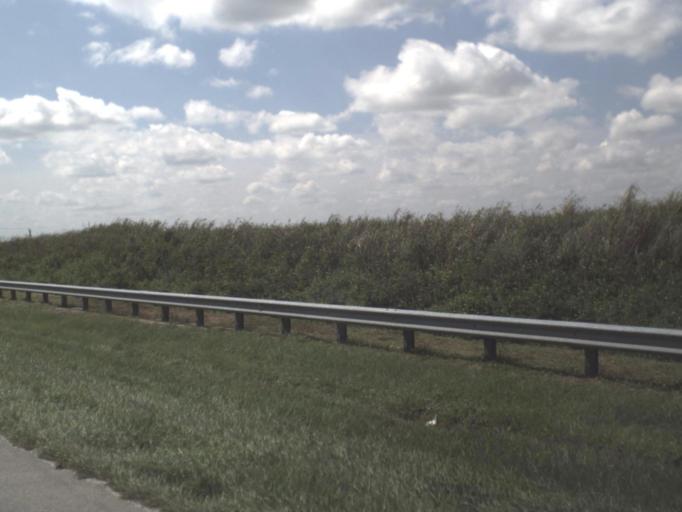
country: US
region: Florida
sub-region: Hendry County
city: LaBelle
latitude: 26.7119
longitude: -81.4374
